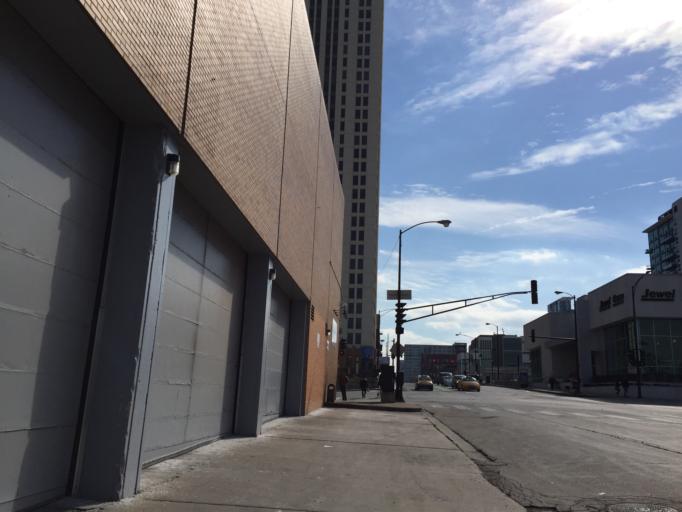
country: US
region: Illinois
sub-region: Cook County
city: Chicago
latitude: 41.8895
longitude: -87.6442
